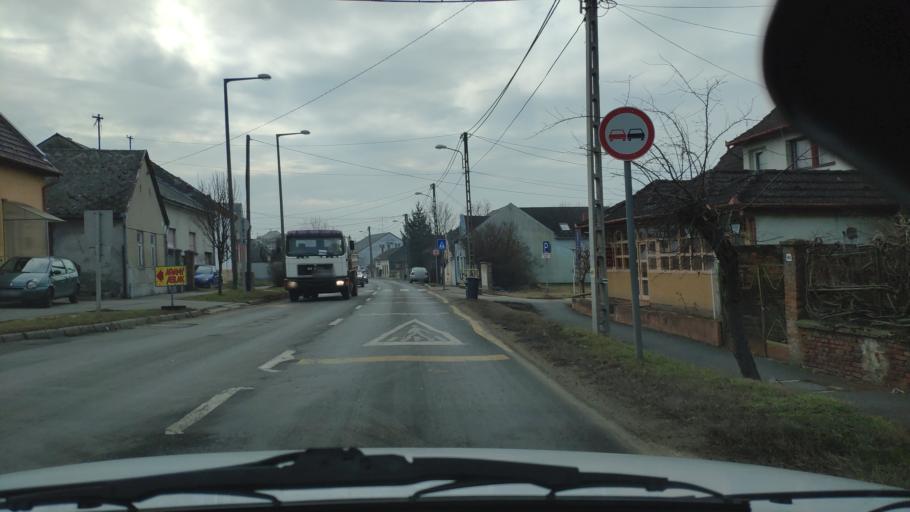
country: HU
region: Zala
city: Nagykanizsa
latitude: 46.4635
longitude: 16.9859
